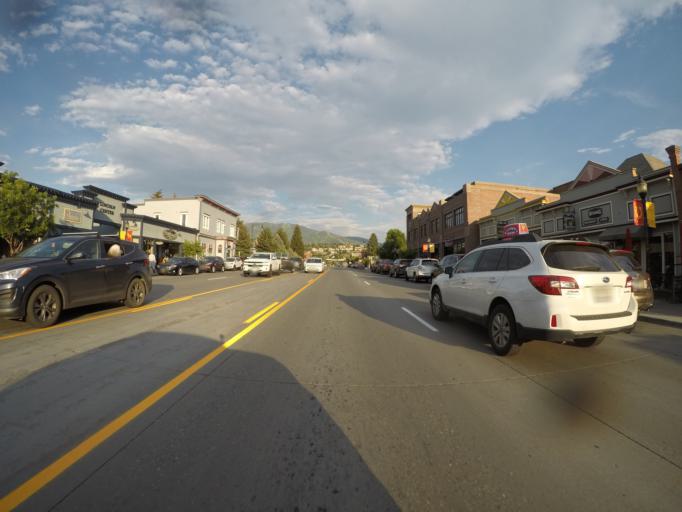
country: US
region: Colorado
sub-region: Routt County
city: Steamboat Springs
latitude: 40.4852
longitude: -106.8331
